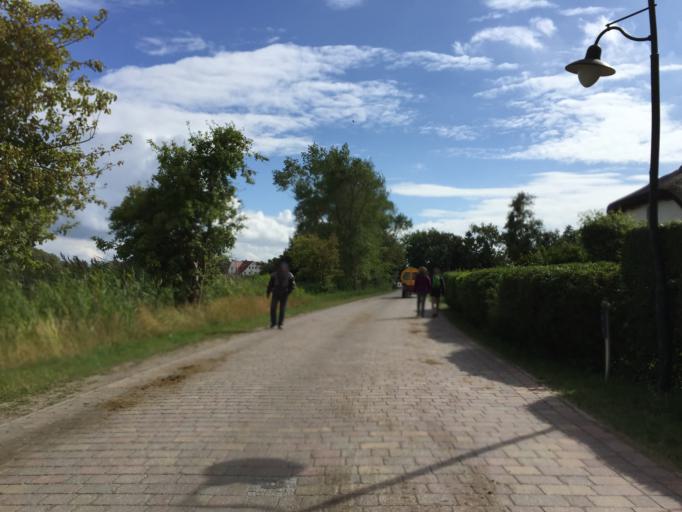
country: DE
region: Mecklenburg-Vorpommern
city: Hiddensee
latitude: 54.5715
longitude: 13.1060
